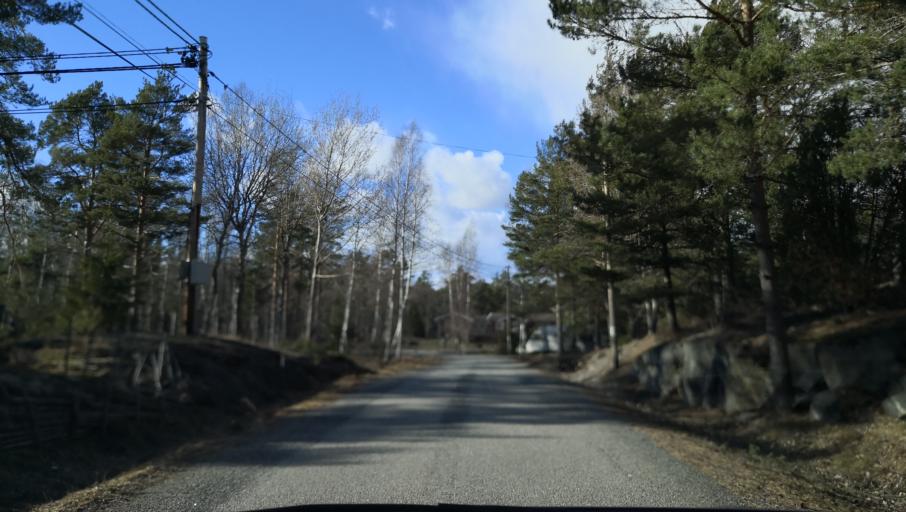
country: SE
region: Stockholm
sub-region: Varmdo Kommun
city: Hemmesta
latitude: 59.2453
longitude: 18.5154
